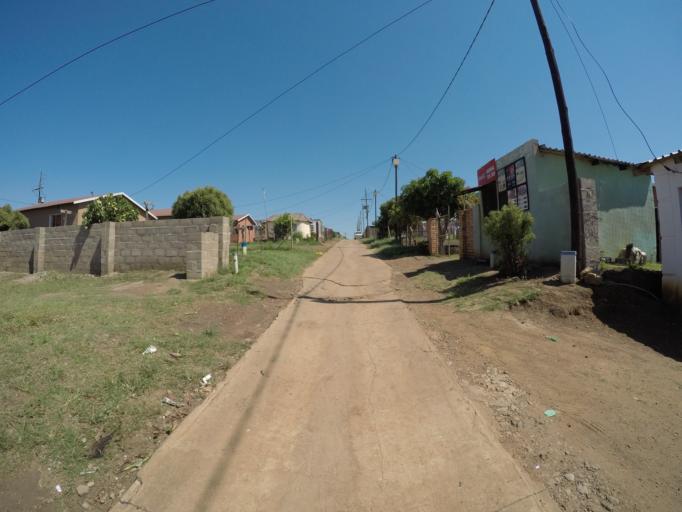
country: ZA
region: KwaZulu-Natal
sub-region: uThungulu District Municipality
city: Empangeni
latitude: -28.7671
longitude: 31.8778
